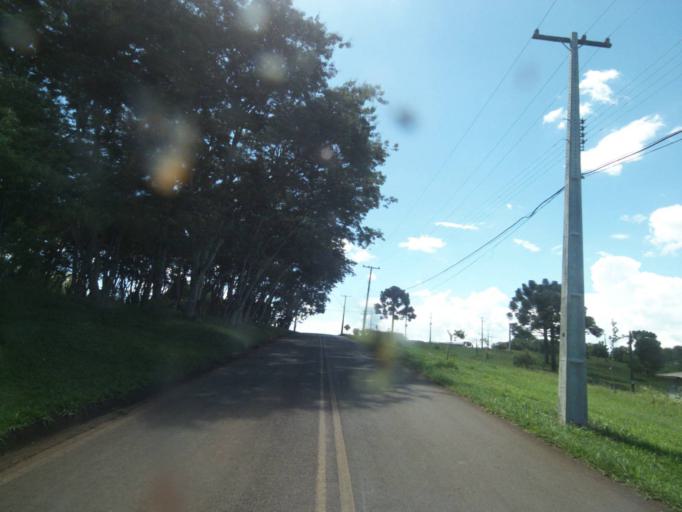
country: BR
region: Parana
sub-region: Pinhao
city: Pinhao
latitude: -25.7923
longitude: -52.0800
